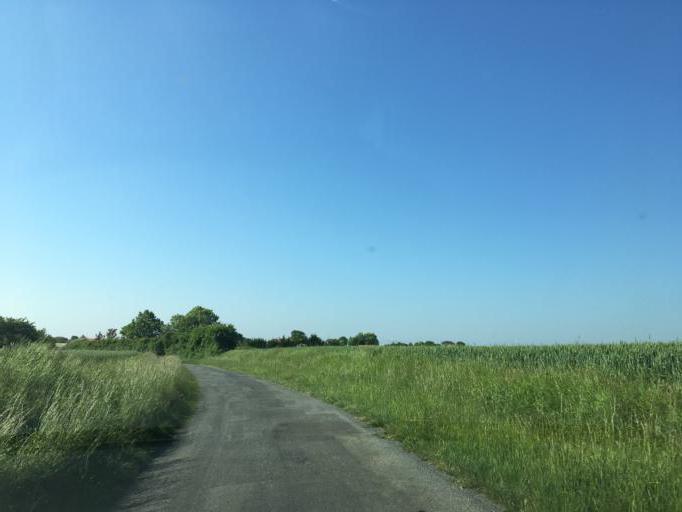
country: FR
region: Poitou-Charentes
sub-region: Departement des Deux-Sevres
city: Beauvoir-sur-Niort
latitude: 46.0790
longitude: -0.5086
